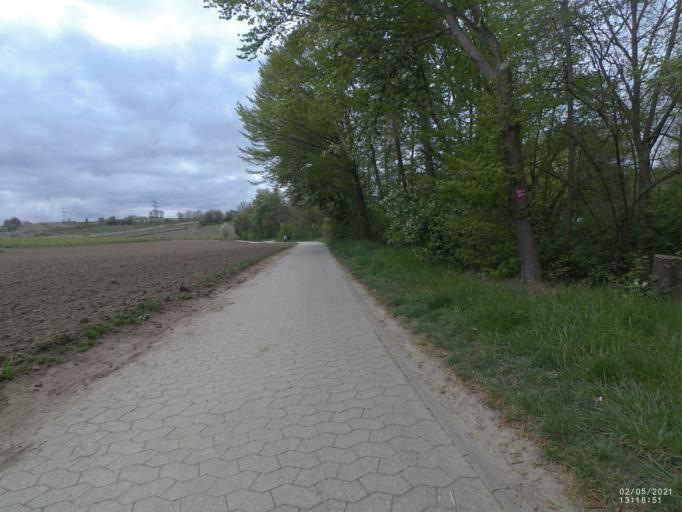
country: DE
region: Rheinland-Pfalz
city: Mulheim-Karlich
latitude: 50.3770
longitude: 7.4893
